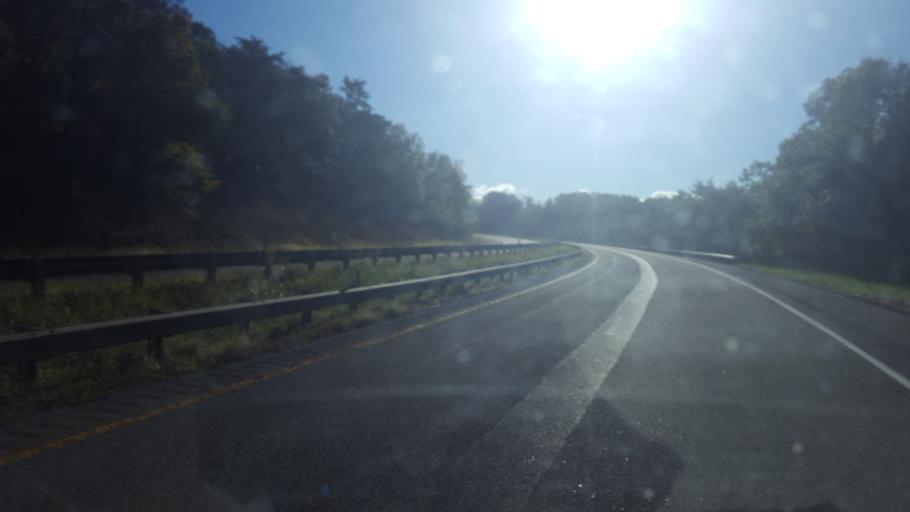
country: US
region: West Virginia
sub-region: Morgan County
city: Berkeley Springs
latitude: 39.6647
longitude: -78.4256
